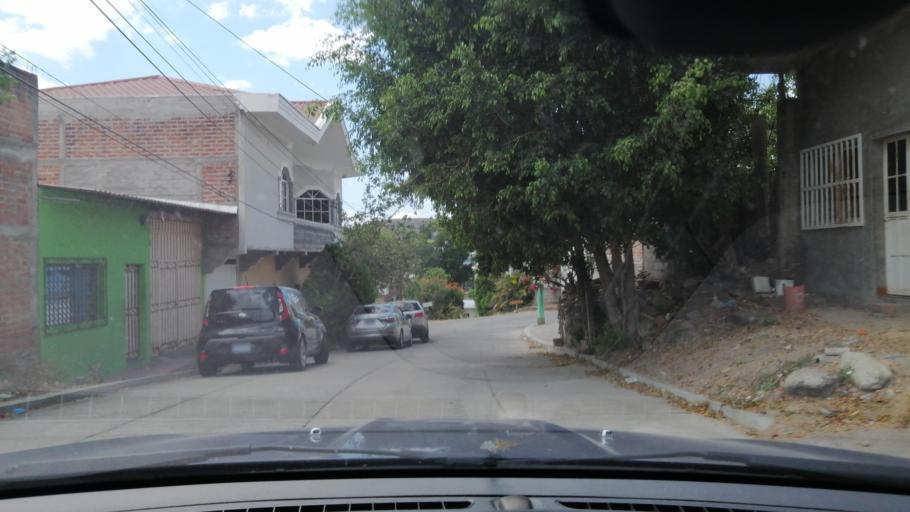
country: SV
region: Santa Ana
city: Metapan
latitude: 14.3331
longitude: -89.4402
